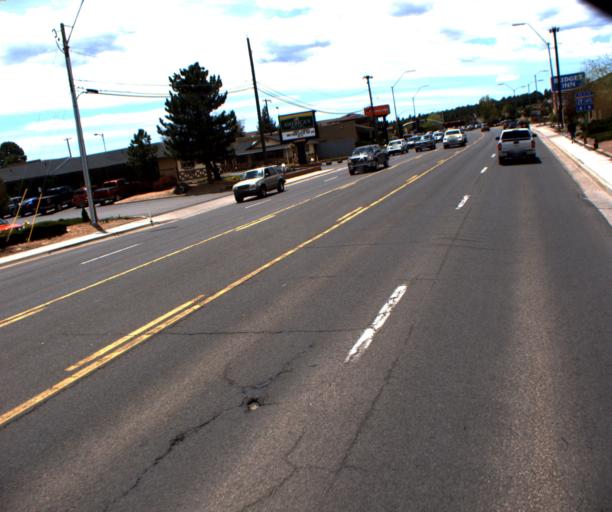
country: US
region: Arizona
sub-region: Coconino County
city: Flagstaff
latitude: 35.1922
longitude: -111.6594
